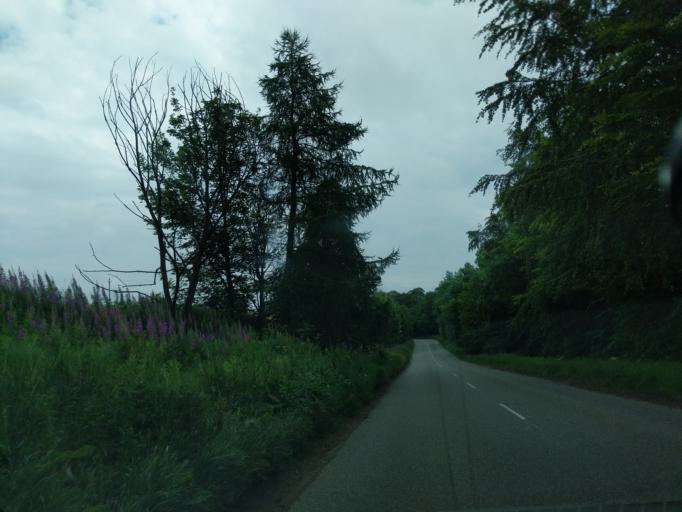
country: GB
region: Scotland
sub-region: Moray
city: Rothes
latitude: 57.4907
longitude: -3.2020
